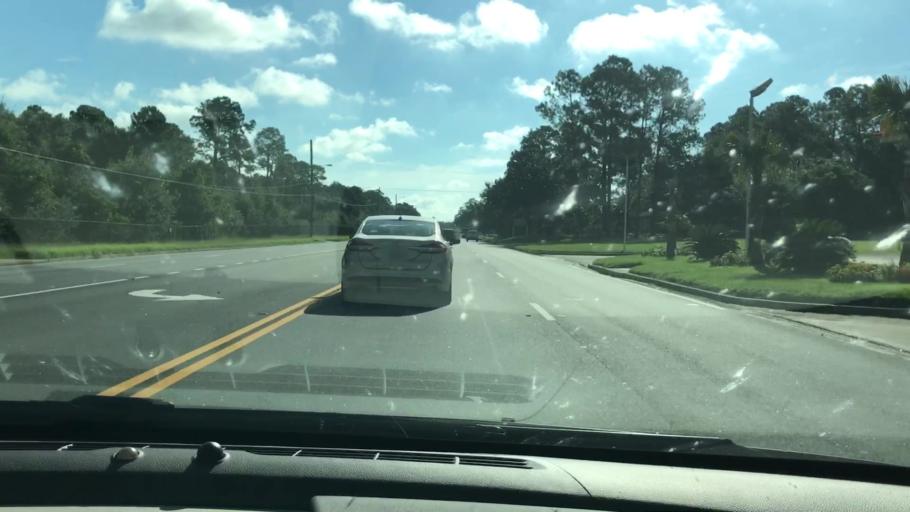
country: US
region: Georgia
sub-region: Dougherty County
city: Albany
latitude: 31.5799
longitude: -84.0943
